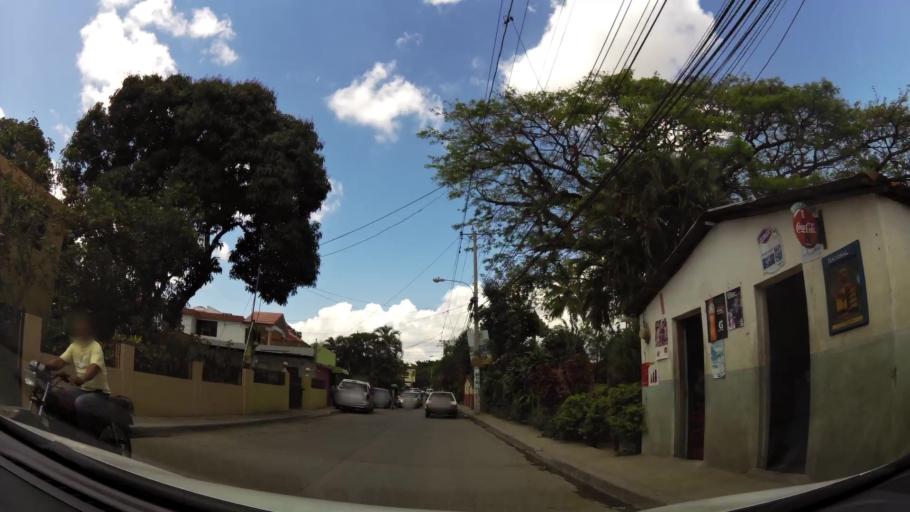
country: DO
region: Santiago
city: Santiago de los Caballeros
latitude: 19.4761
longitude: -70.6689
